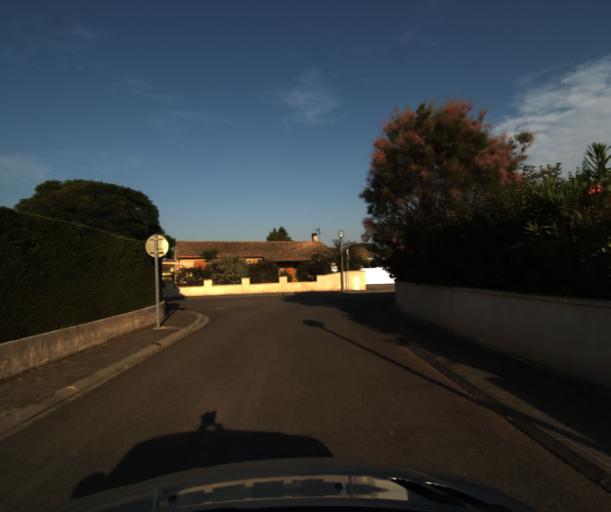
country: FR
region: Midi-Pyrenees
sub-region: Departement de la Haute-Garonne
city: Roquettes
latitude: 43.4825
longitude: 1.3807
